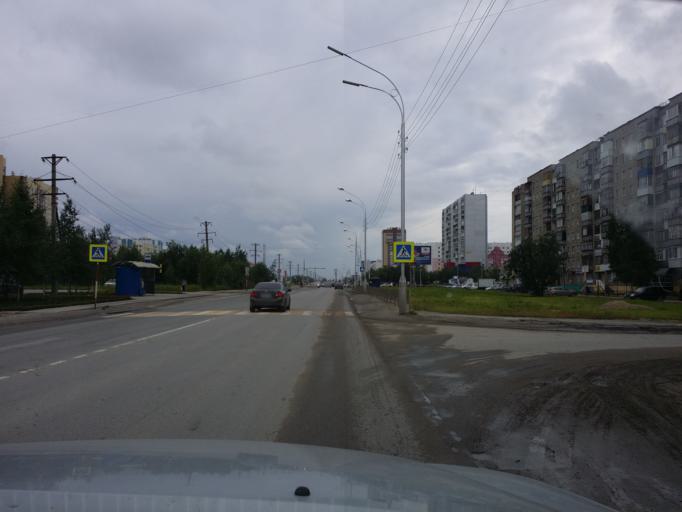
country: RU
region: Khanty-Mansiyskiy Avtonomnyy Okrug
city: Nizhnevartovsk
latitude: 60.9321
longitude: 76.6099
